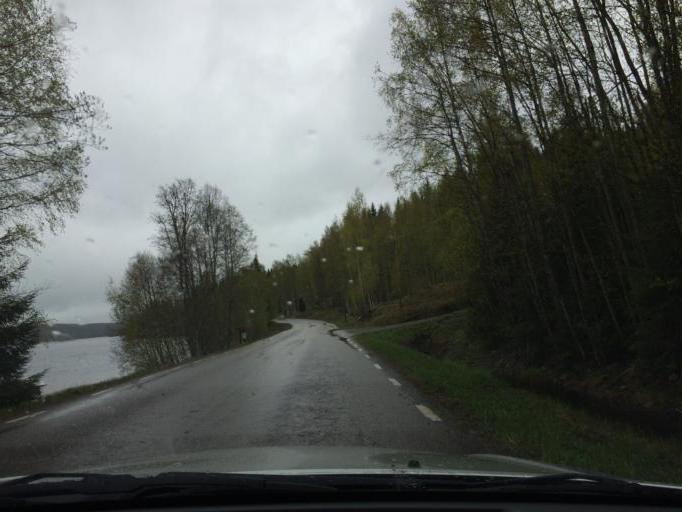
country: SE
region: Dalarna
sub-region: Ludvika Kommun
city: Grangesberg
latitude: 60.0573
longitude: 14.8861
